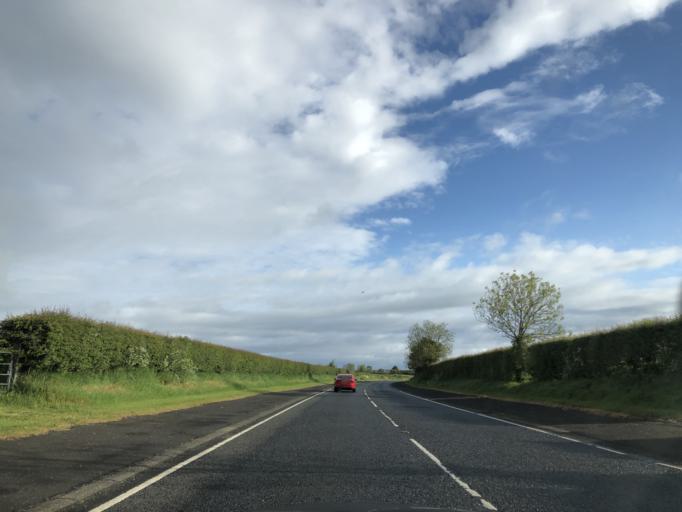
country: GB
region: Northern Ireland
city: Bushmills
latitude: 55.1572
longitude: -6.5750
